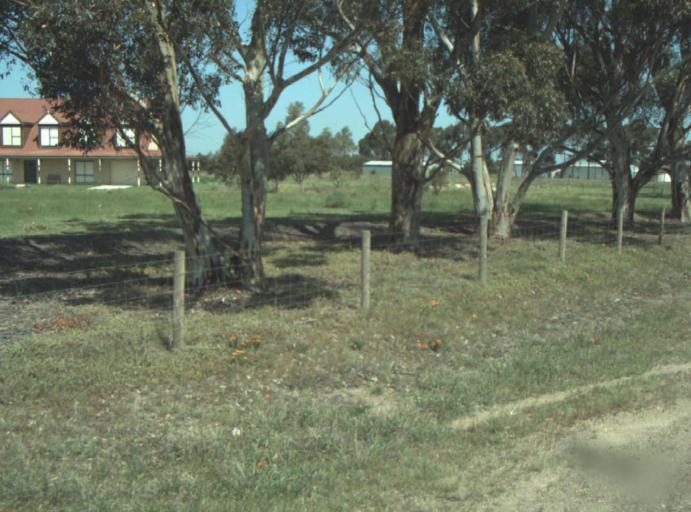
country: AU
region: Victoria
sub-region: Greater Geelong
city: Lara
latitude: -37.9760
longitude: 144.4048
